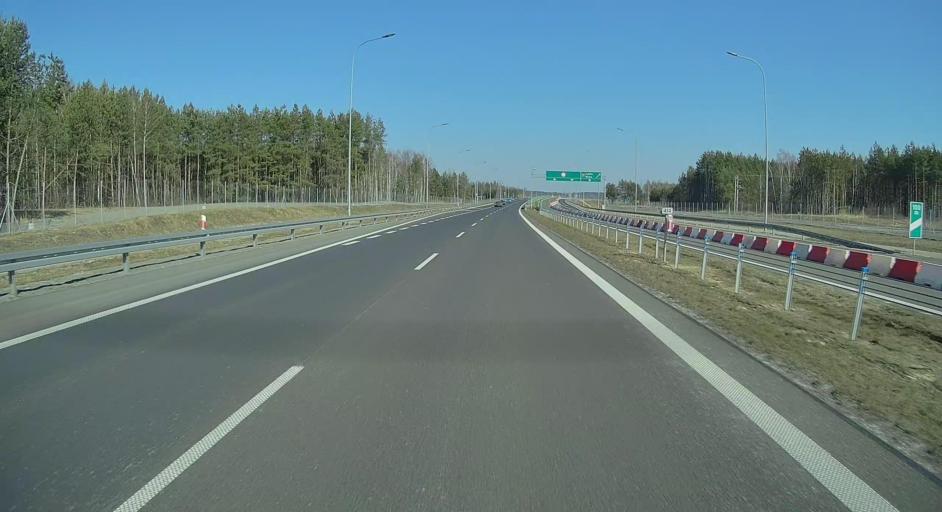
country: PL
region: Subcarpathian Voivodeship
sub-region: Powiat nizanski
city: Przedzel
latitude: 50.4912
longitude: 22.1926
